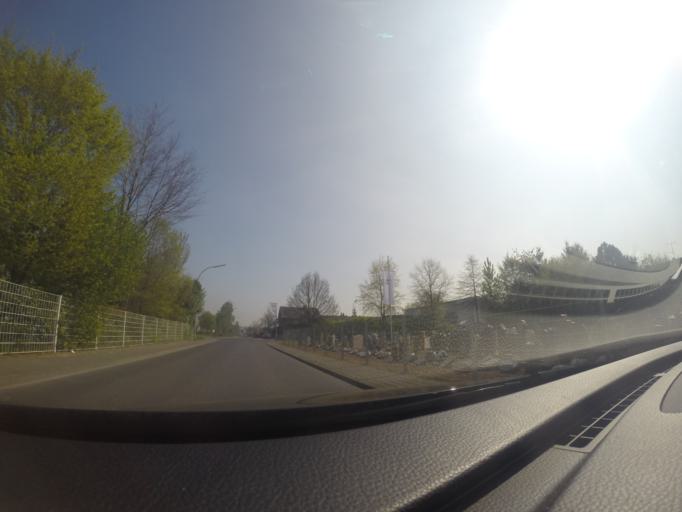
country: DE
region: North Rhine-Westphalia
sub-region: Regierungsbezirk Dusseldorf
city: Xanten
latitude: 51.6599
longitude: 6.4406
